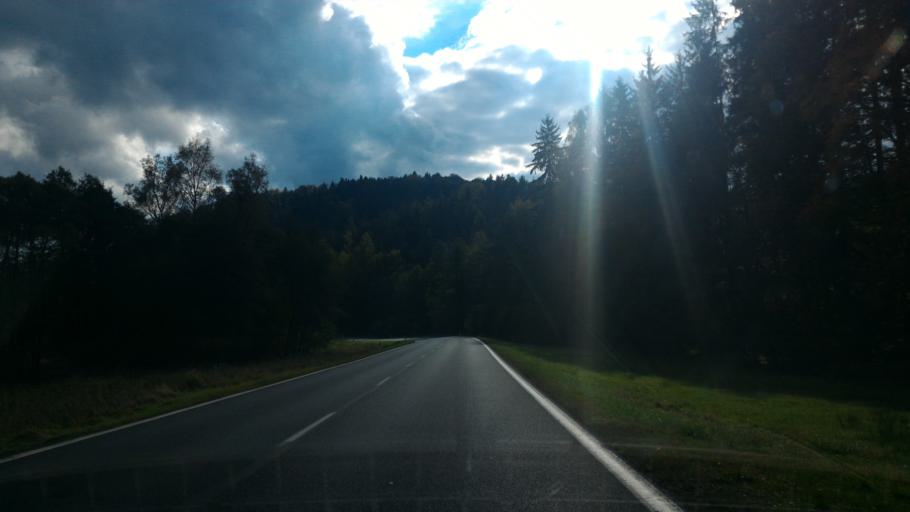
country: CZ
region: Ustecky
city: Ceska Kamenice
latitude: 50.8138
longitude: 14.4395
